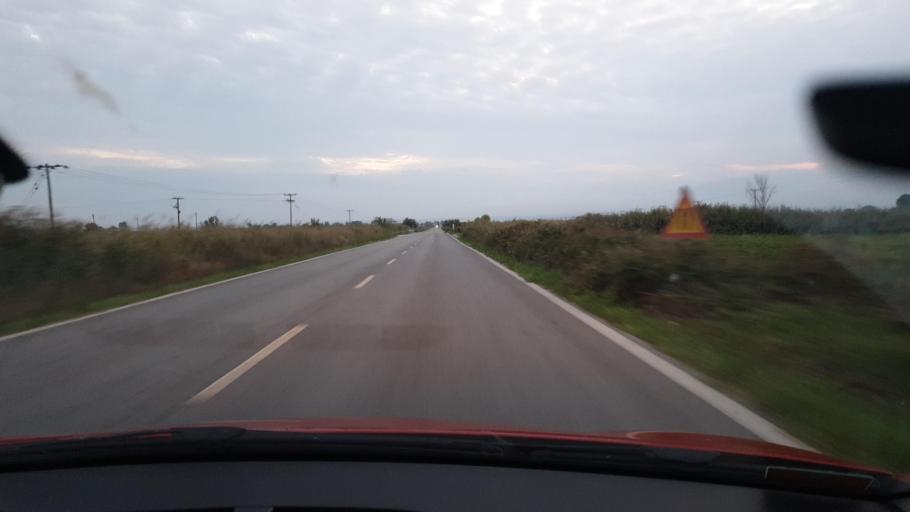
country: GR
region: Central Macedonia
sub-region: Nomos Kilkis
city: Polykastro
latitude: 40.9989
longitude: 22.6317
